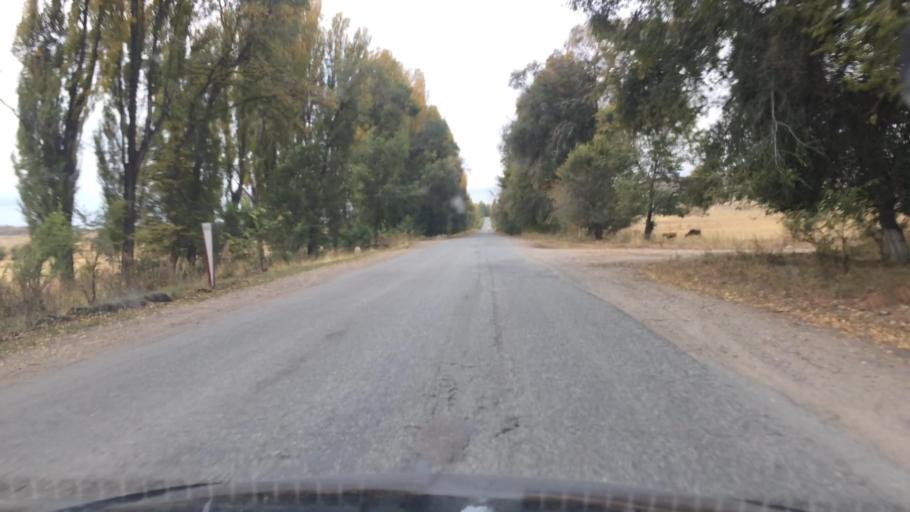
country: KG
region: Ysyk-Koel
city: Pokrovka
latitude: 42.7394
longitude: 77.8971
